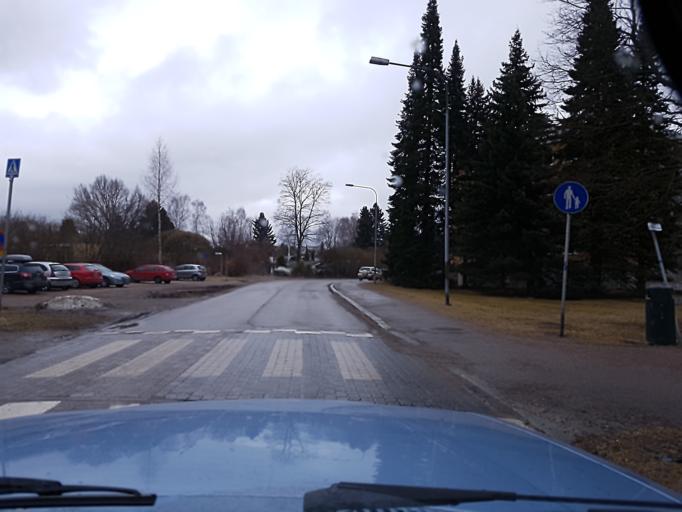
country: FI
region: Uusimaa
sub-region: Helsinki
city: Otaniemi
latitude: 60.1813
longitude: 24.7997
